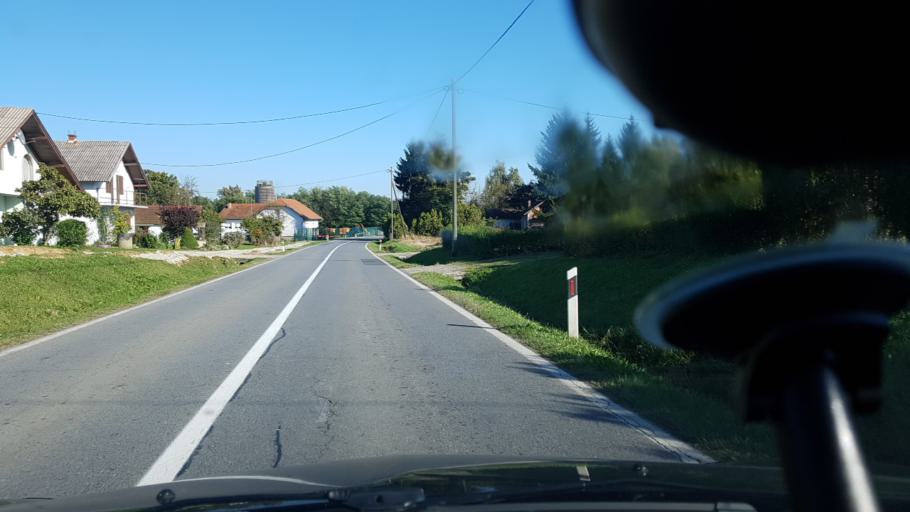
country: HR
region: Bjelovarsko-Bilogorska
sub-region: Grad Cazma
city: Cazma
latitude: 45.7843
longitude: 16.6554
